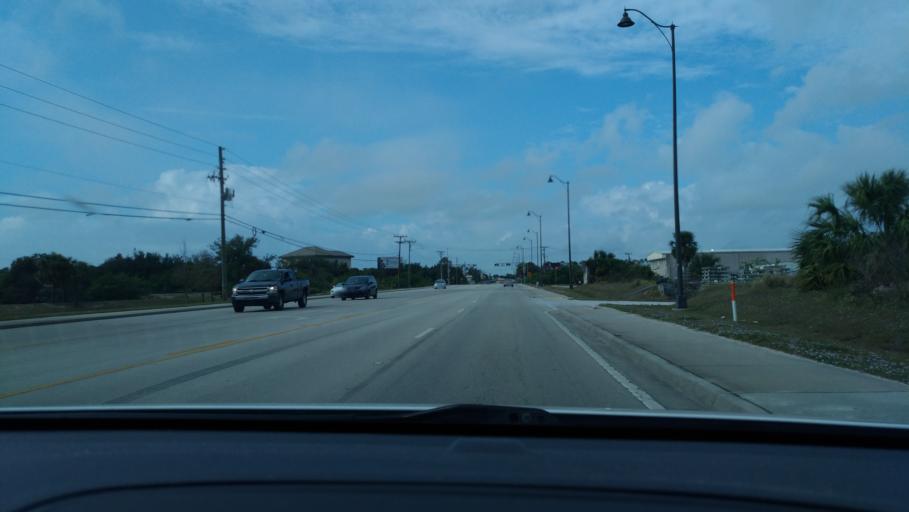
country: US
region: Florida
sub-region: Lee County
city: Bonita Springs
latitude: 26.3747
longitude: -81.8025
